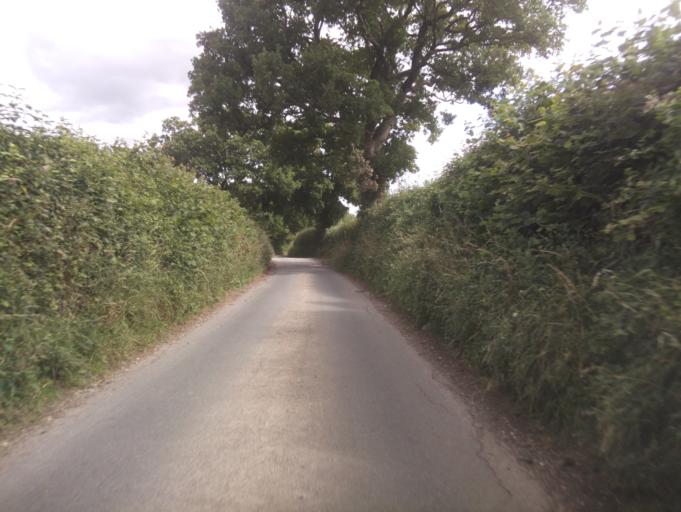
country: GB
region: England
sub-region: Gloucestershire
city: Newent
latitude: 51.8471
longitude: -2.3962
